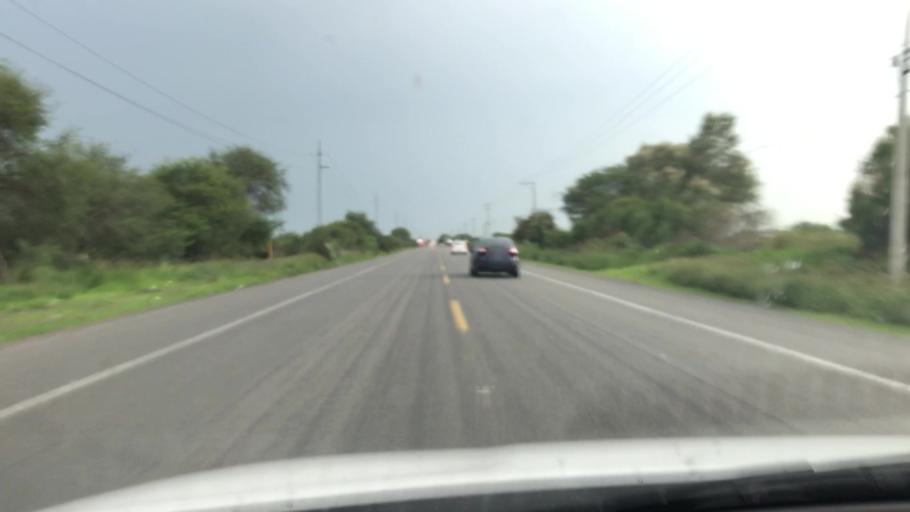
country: MX
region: Michoacan
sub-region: Vista Hermosa
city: Los Pilares
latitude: 20.2749
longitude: -102.4003
